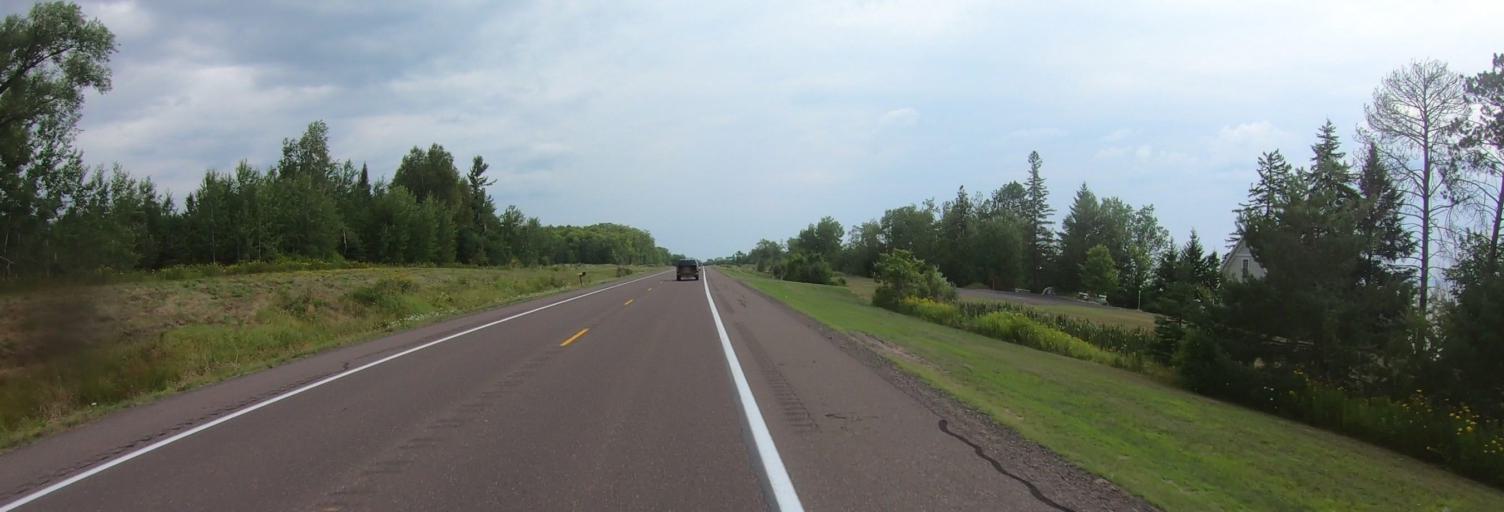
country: US
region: Michigan
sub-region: Baraga County
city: Baraga
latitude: 46.8629
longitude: -88.4807
